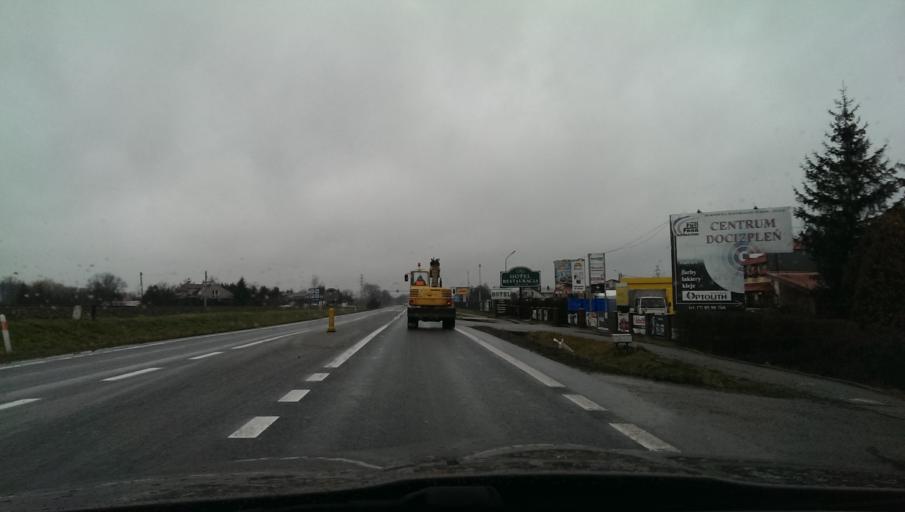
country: PL
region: Subcarpathian Voivodeship
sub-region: Powiat rzeszowski
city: Rudna Mala
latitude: 50.0853
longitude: 21.9839
